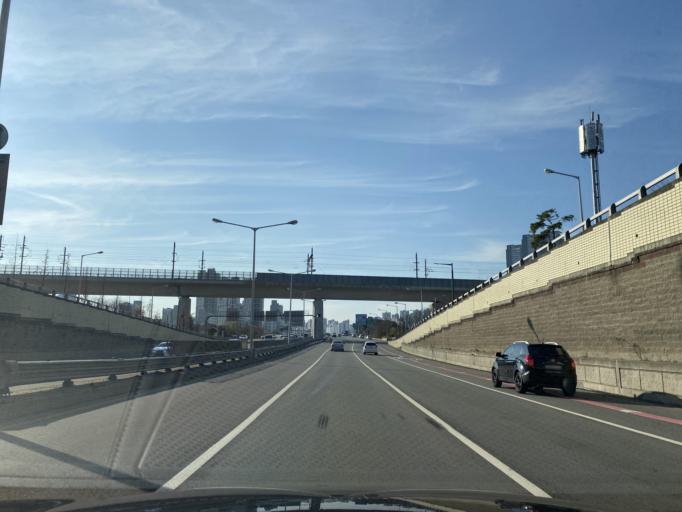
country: KR
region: Chungcheongnam-do
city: Cheonan
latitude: 36.7844
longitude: 127.1090
